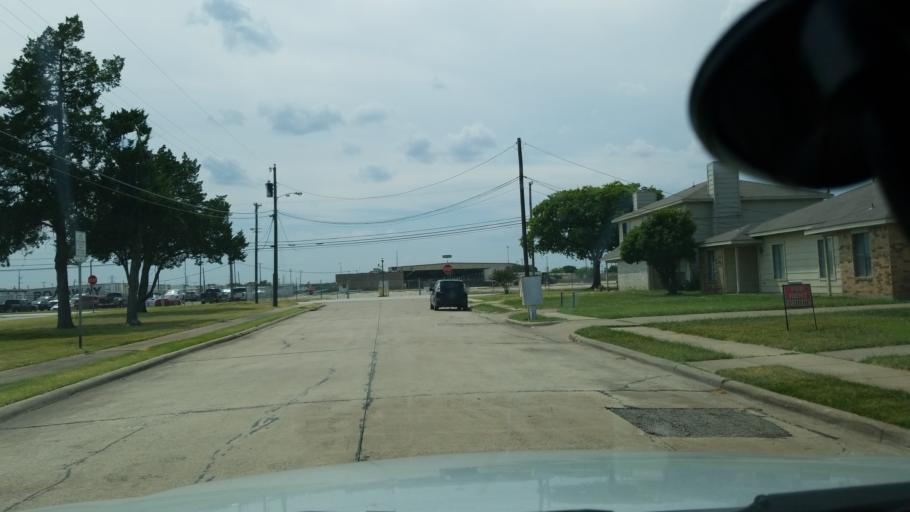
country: US
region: Texas
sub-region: Dallas County
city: Irving
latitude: 32.8187
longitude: -96.9888
